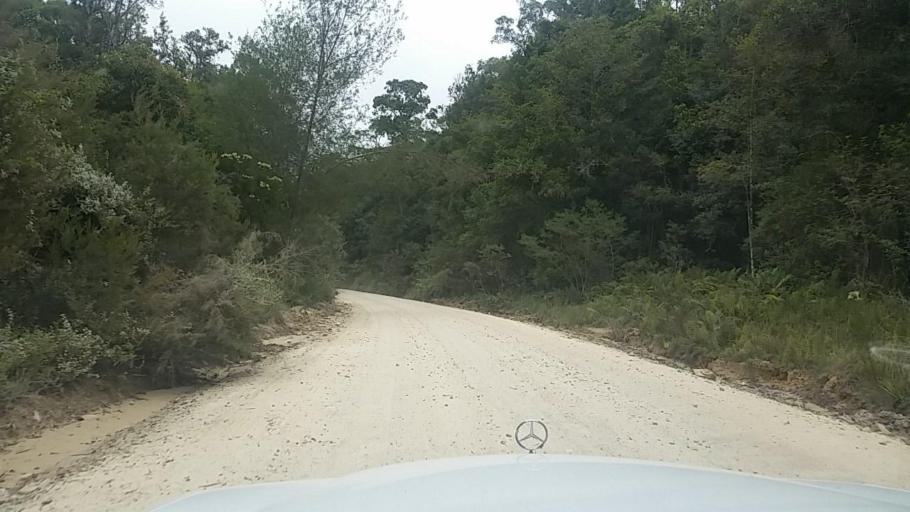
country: ZA
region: Western Cape
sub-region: Eden District Municipality
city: Knysna
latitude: -33.9674
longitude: 23.1495
